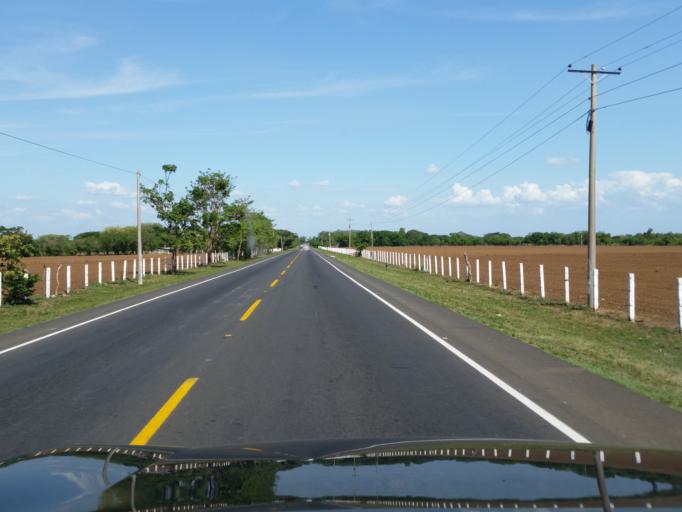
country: NI
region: Leon
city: Leon
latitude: 12.3549
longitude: -86.8324
